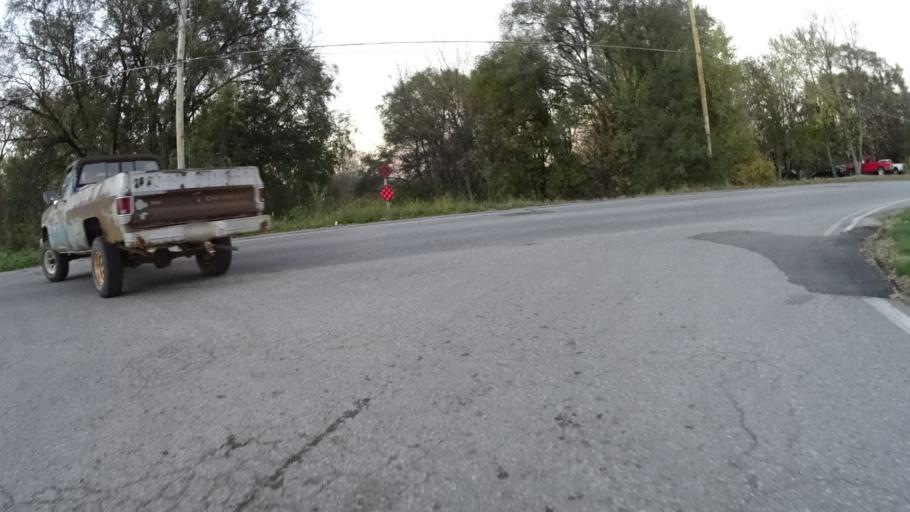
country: US
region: Nebraska
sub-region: Sarpy County
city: Offutt Air Force Base
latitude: 41.1836
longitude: -95.9525
